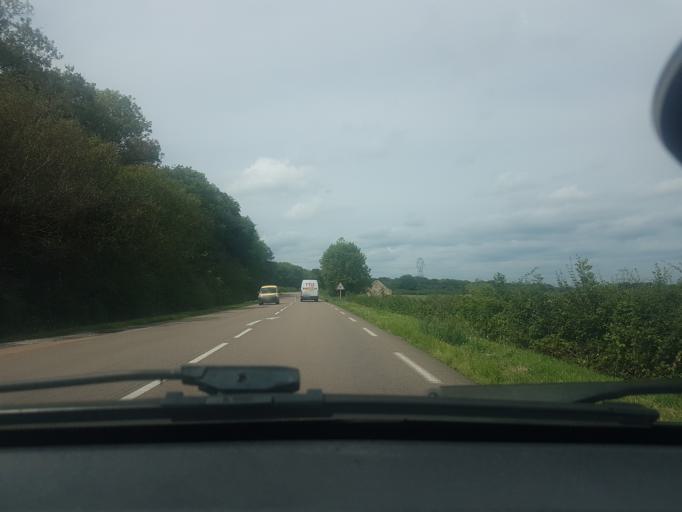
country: FR
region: Bourgogne
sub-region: Departement de la Cote-d'Or
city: Nolay
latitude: 47.0382
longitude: 4.6199
